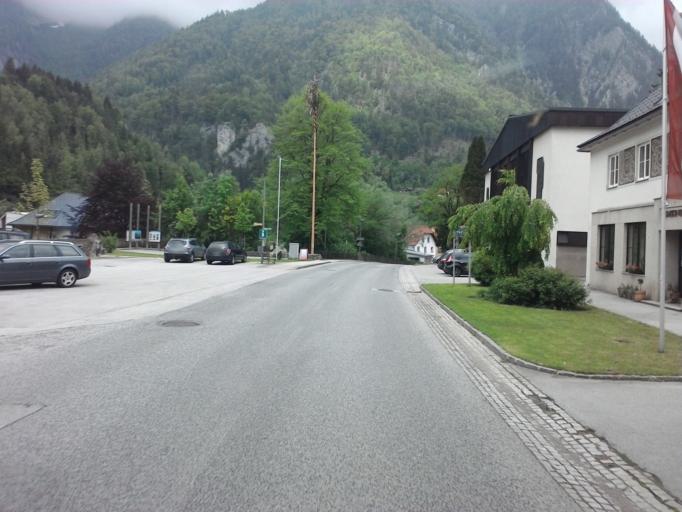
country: AT
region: Styria
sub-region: Politischer Bezirk Leoben
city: Hieflau
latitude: 47.6058
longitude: 14.7448
